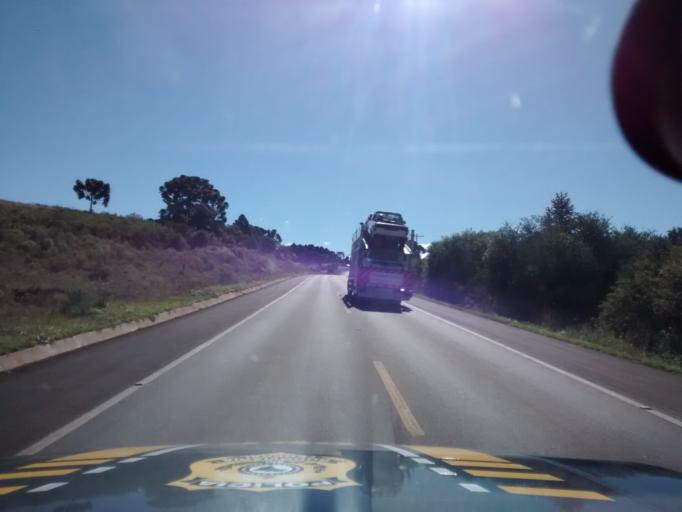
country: BR
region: Rio Grande do Sul
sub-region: Vacaria
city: Vacaria
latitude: -28.3648
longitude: -51.1021
